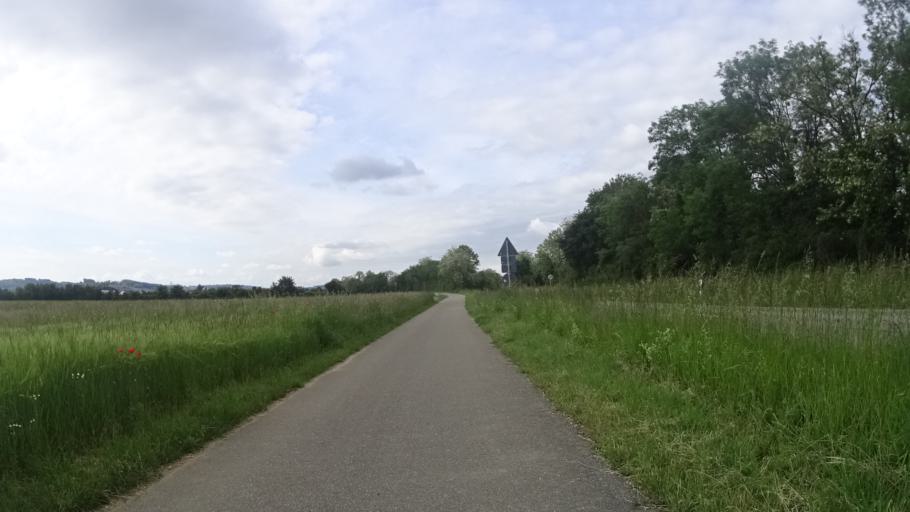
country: DE
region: Baden-Wuerttemberg
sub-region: Freiburg Region
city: Schliengen
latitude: 47.7779
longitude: 7.5535
